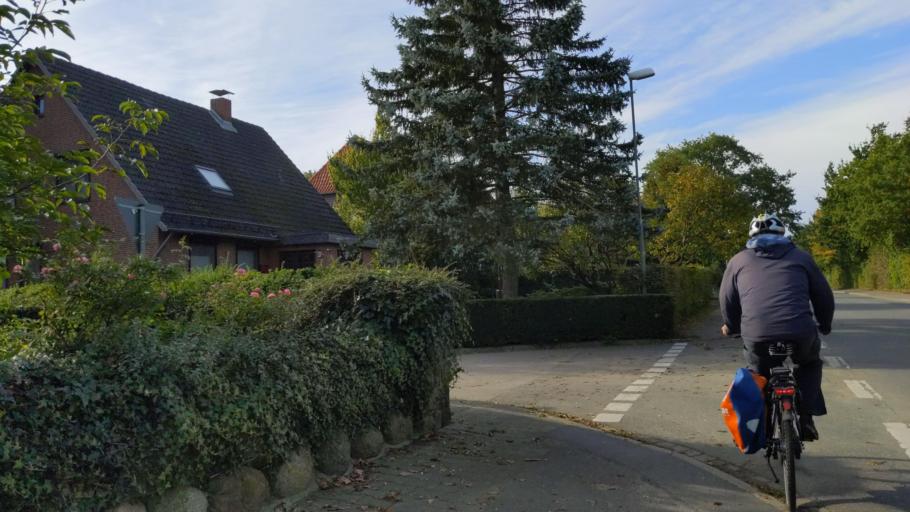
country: DE
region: Schleswig-Holstein
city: Badendorf
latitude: 53.8659
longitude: 10.5767
